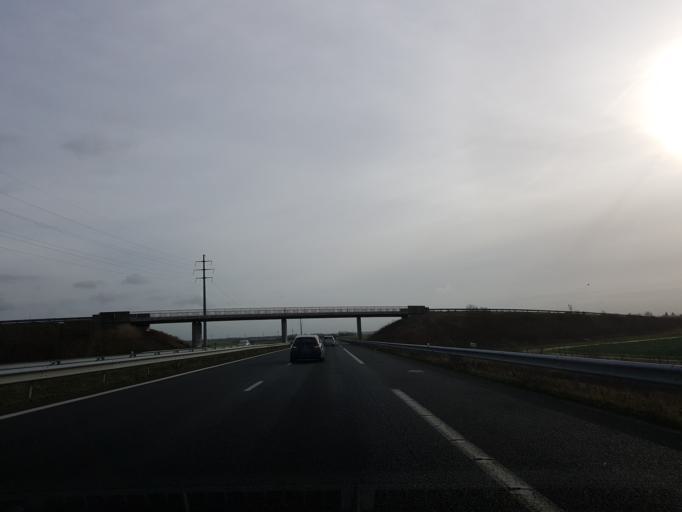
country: FR
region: Champagne-Ardenne
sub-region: Departement de l'Aube
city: Saint-Germain
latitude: 48.2490
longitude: 3.9868
